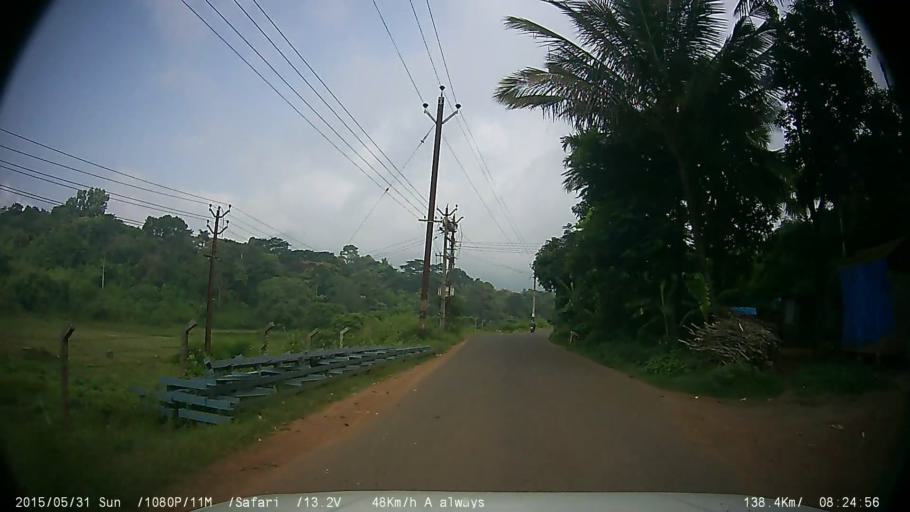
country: IN
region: Kerala
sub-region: Wayanad
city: Kalpetta
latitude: 11.6741
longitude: 75.9614
